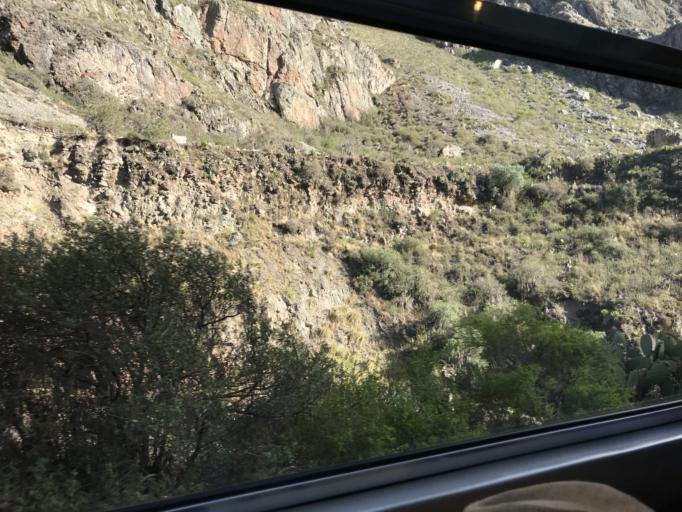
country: PE
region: Cusco
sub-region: Provincia de Urubamba
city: Ollantaytambo
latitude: -13.2167
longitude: -72.3855
